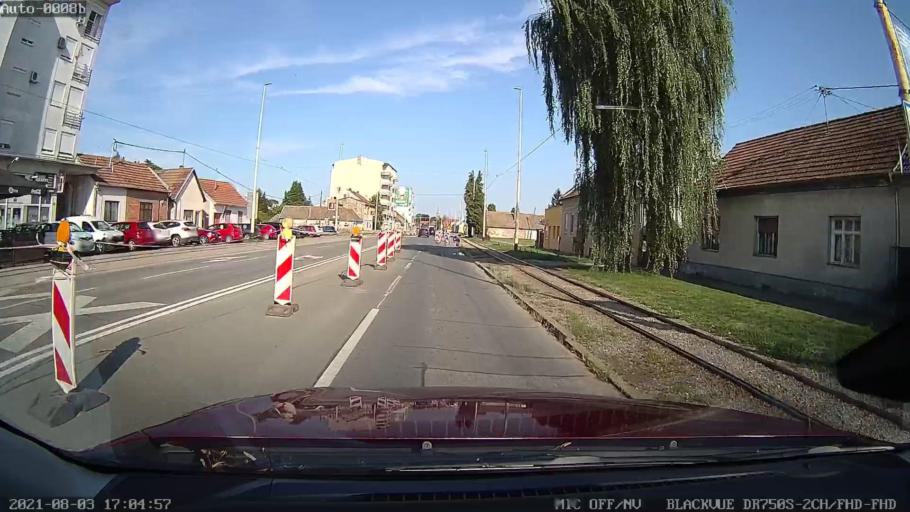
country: HR
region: Osjecko-Baranjska
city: Visnjevac
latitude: 45.5643
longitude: 18.6539
